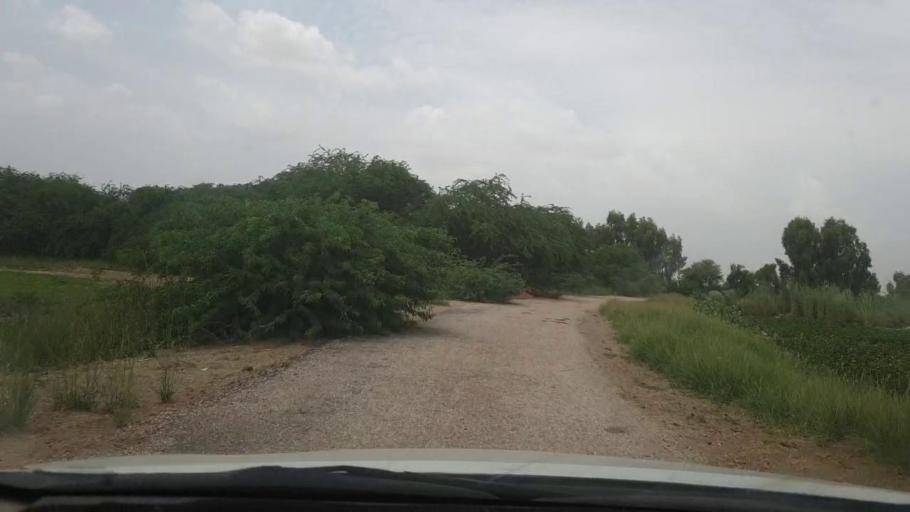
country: PK
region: Sindh
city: Khairpur
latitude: 27.3717
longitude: 68.9857
